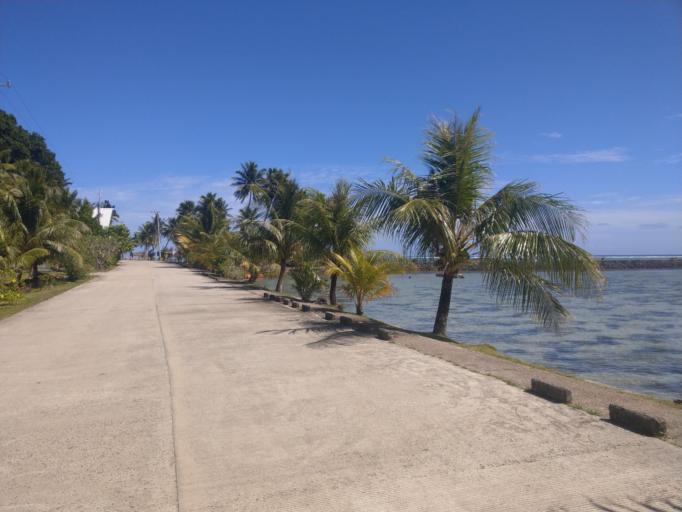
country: PW
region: Melekeok
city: Melekeok Village
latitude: 7.4915
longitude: 134.6361
